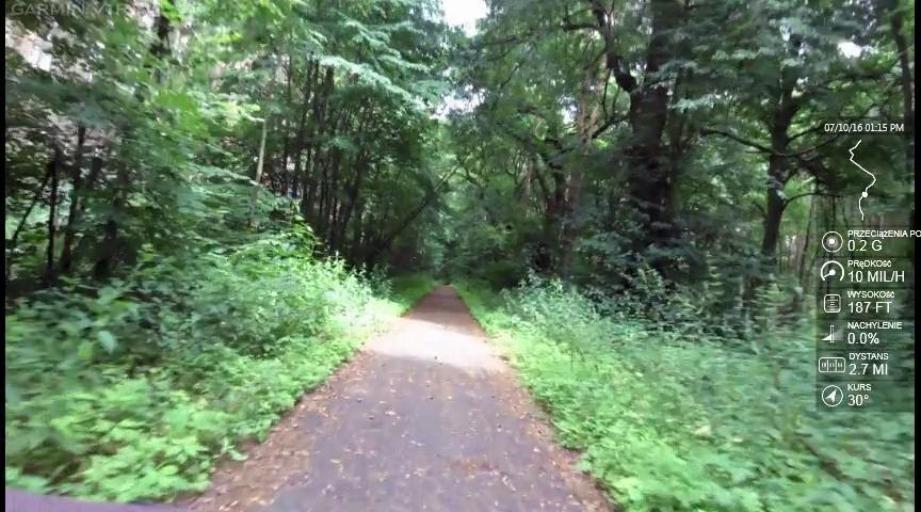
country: PL
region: West Pomeranian Voivodeship
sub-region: Powiat gryfinski
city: Banie
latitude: 53.0750
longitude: 14.6346
